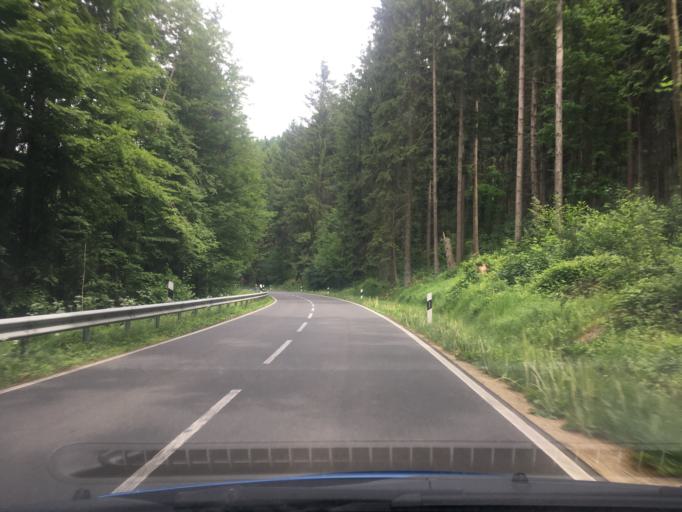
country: DE
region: Lower Saxony
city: Dassel
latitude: 51.7453
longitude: 9.6556
